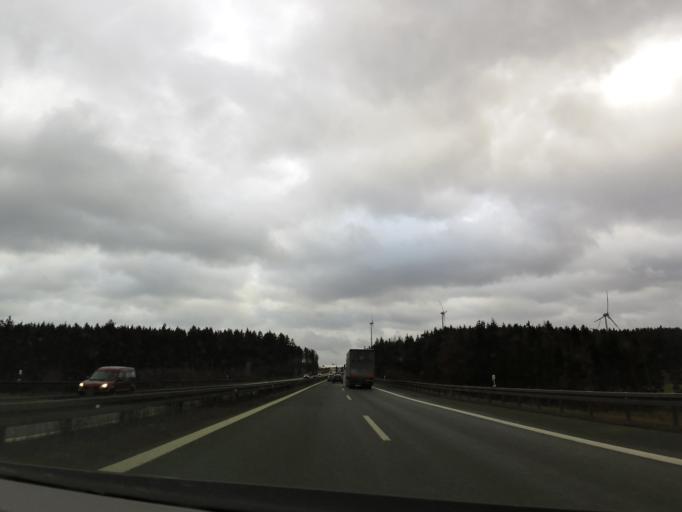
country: DE
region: Bavaria
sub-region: Upper Franconia
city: Gattendorf
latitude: 50.3194
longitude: 12.0237
